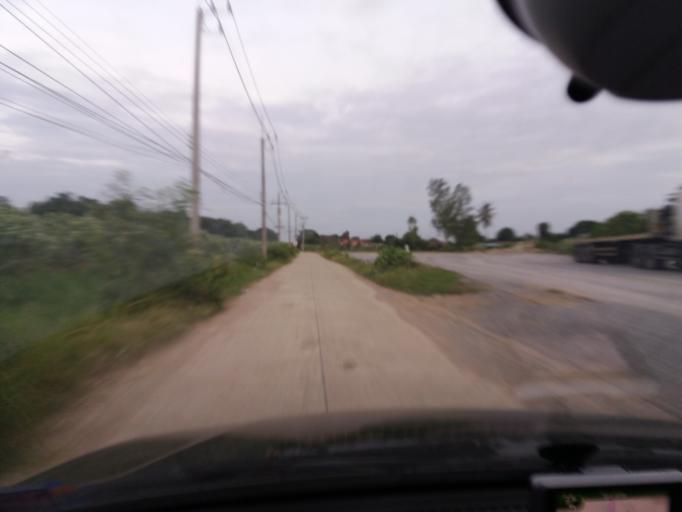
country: TH
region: Suphan Buri
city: Ban Sam Chuk
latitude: 14.7196
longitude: 100.0624
